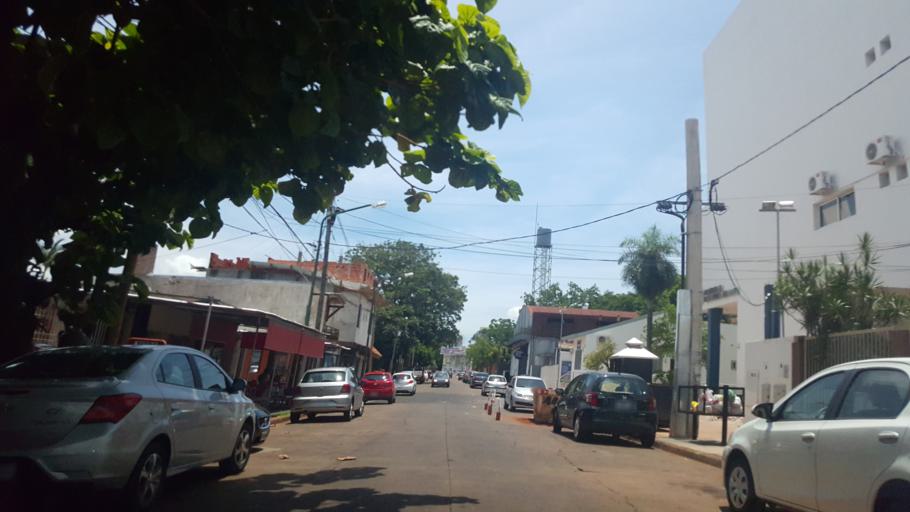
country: AR
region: Misiones
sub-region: Departamento de Capital
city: Posadas
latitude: -27.3753
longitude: -55.9004
